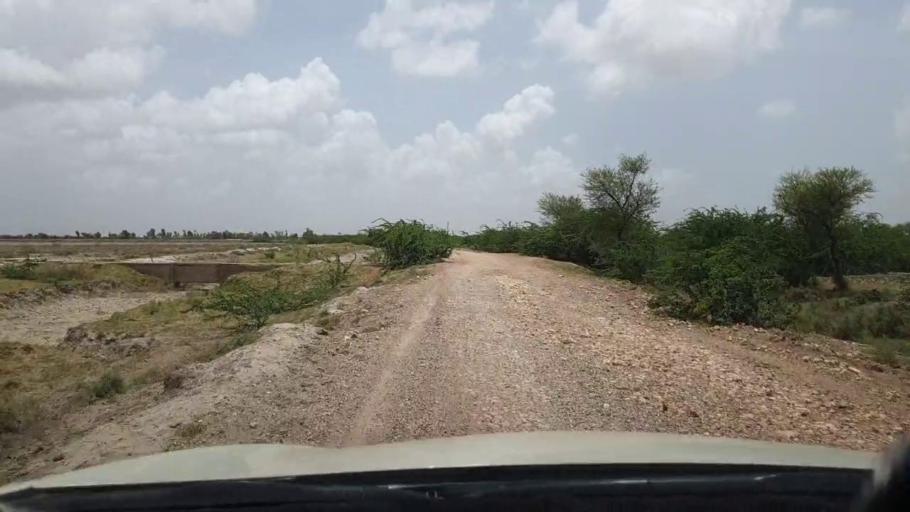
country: PK
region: Sindh
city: Kadhan
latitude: 24.3640
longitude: 68.9267
